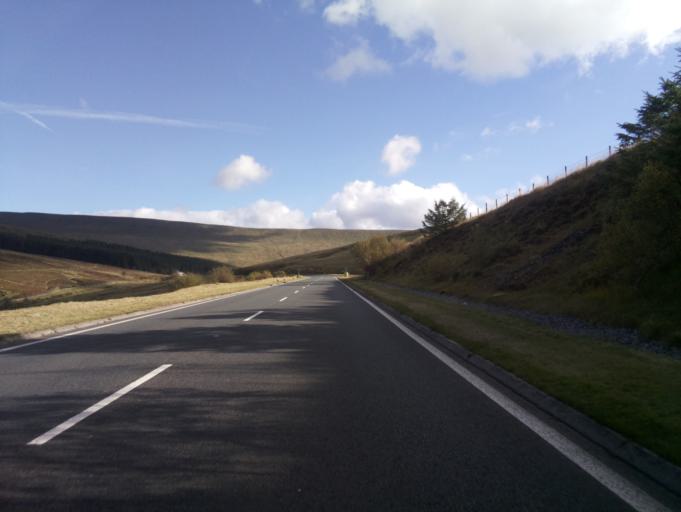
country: GB
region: Wales
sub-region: Sir Powys
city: Brecon
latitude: 51.8738
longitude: -3.4897
